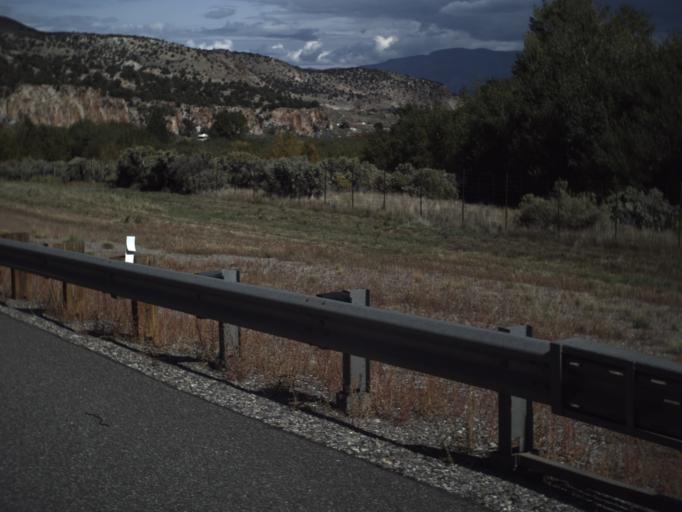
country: US
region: Utah
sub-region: Sevier County
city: Monroe
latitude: 38.5745
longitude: -112.3479
